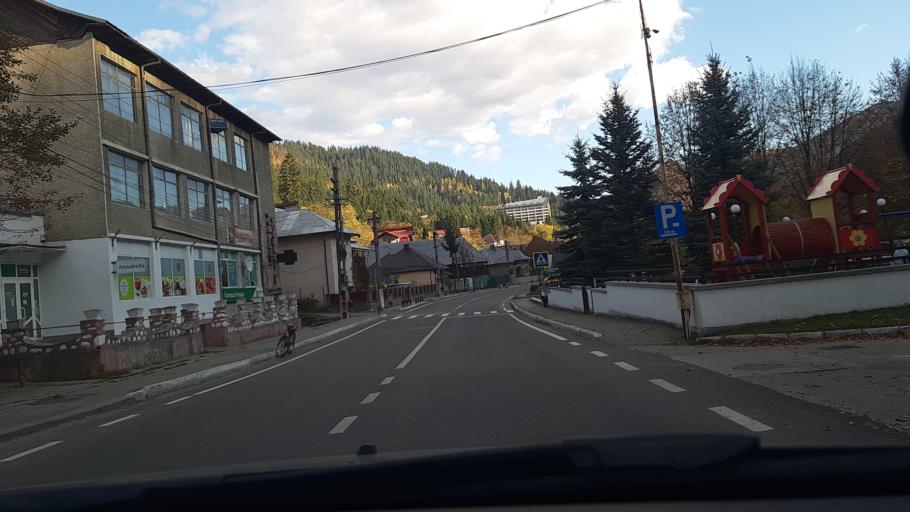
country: RO
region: Valcea
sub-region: Comuna Voineasa
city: Voineasa
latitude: 45.4198
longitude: 23.9558
